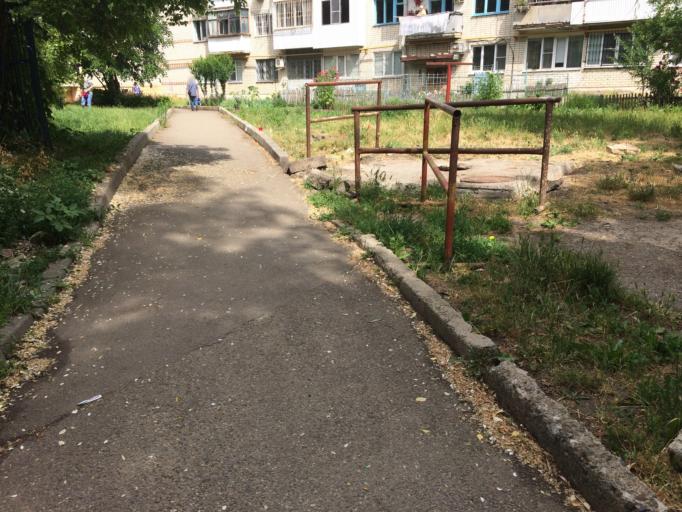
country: RU
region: Stavropol'skiy
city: Stavropol'
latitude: 45.0415
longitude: 41.9526
